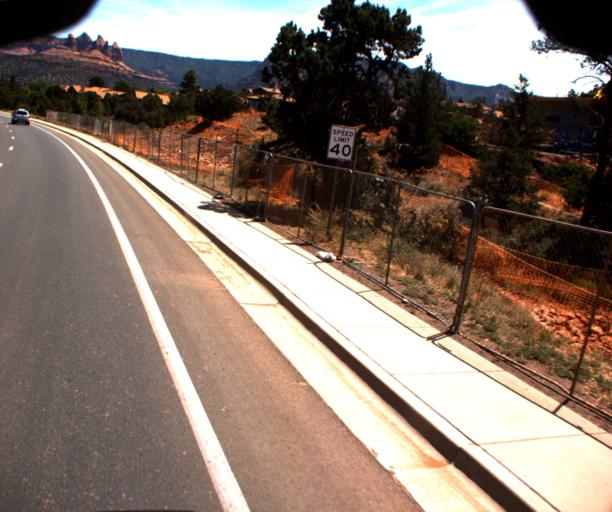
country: US
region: Arizona
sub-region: Coconino County
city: Sedona
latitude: 34.8626
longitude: -111.7801
